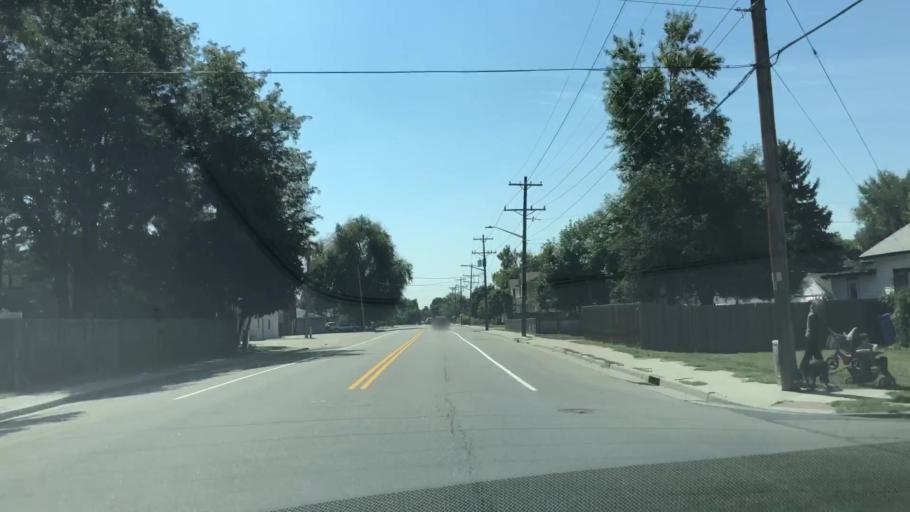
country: US
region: Colorado
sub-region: Larimer County
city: Loveland
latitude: 40.3956
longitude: -105.0589
